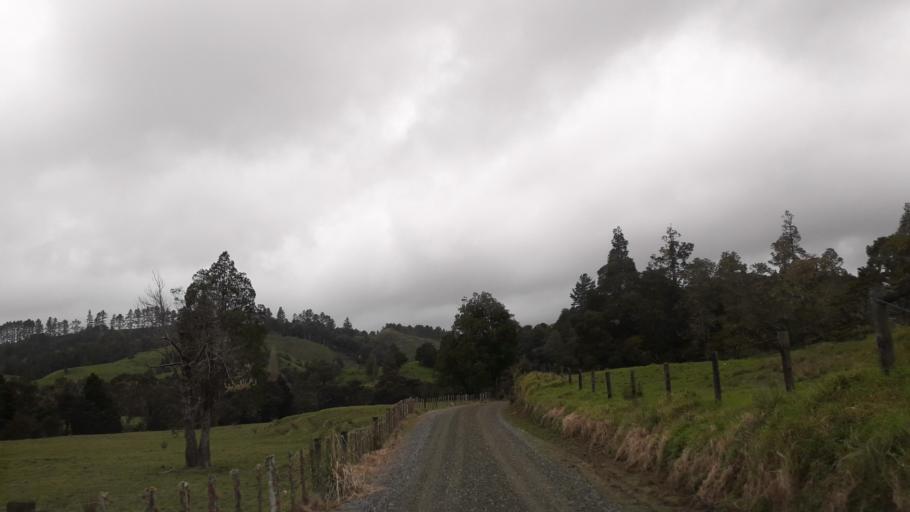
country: NZ
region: Northland
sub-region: Far North District
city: Waimate North
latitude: -35.1563
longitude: 173.7131
